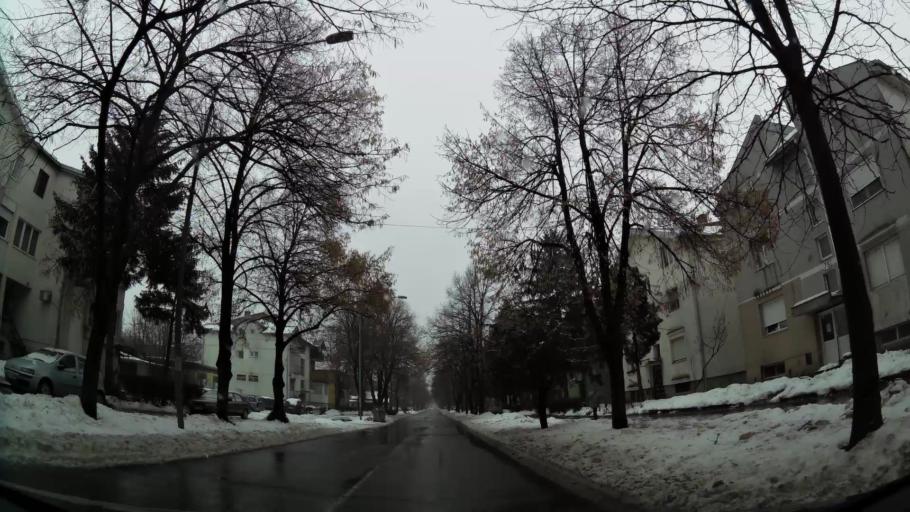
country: RS
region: Central Serbia
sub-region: Belgrade
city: Zemun
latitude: 44.8754
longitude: 20.3195
